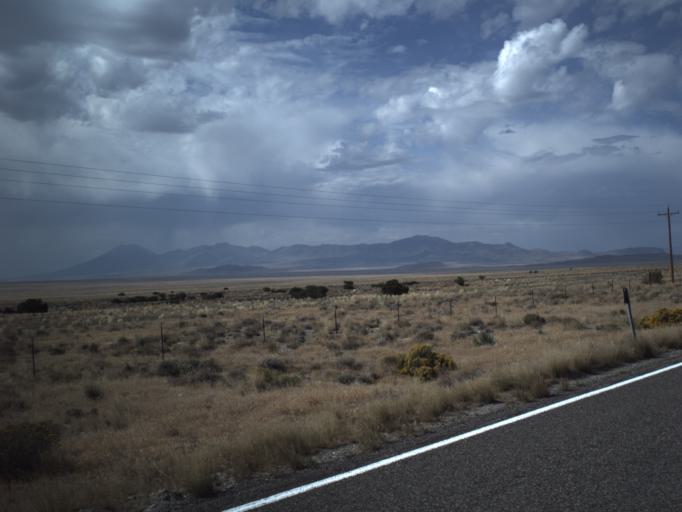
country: US
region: Utah
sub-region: Tooele County
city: Wendover
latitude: 41.4367
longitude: -113.7451
